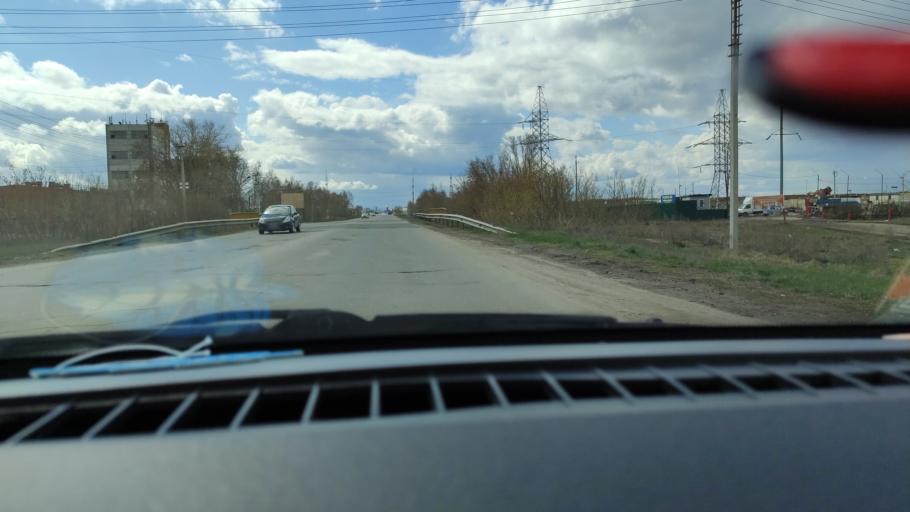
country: RU
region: Samara
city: Tol'yatti
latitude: 53.5818
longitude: 49.4038
